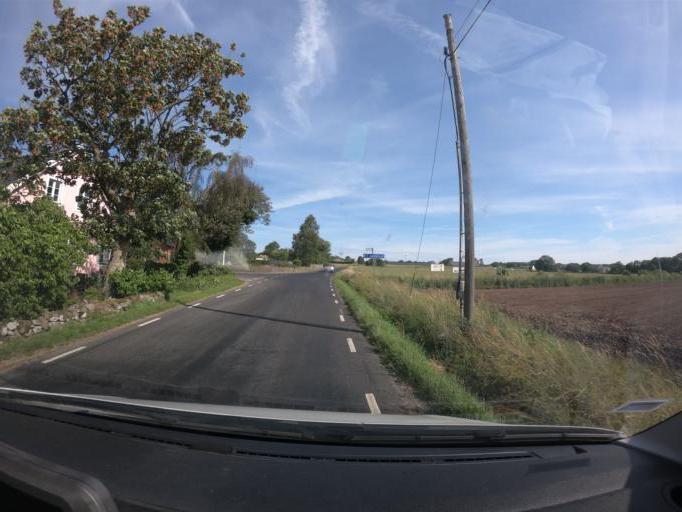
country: SE
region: Skane
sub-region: Angelholms Kommun
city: Vejbystrand
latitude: 56.3970
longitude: 12.7023
